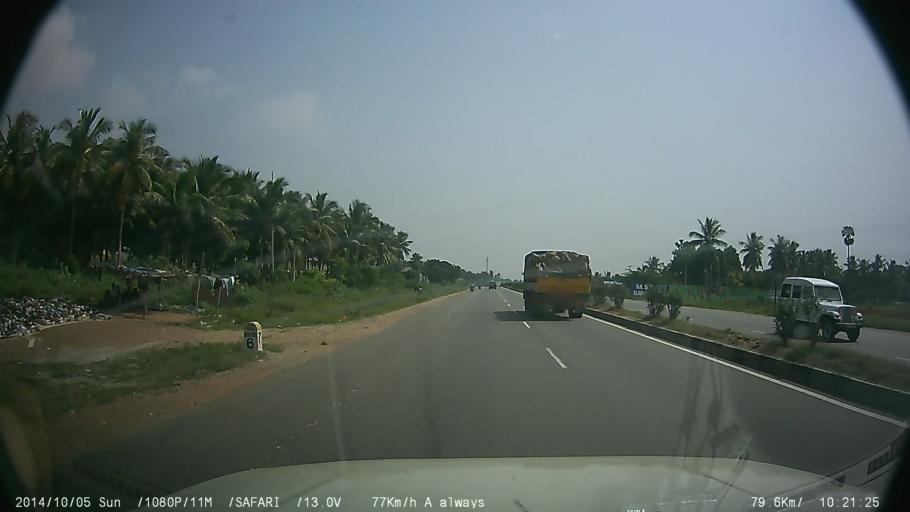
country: IN
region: Tamil Nadu
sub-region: Salem
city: Attayyampatti
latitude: 11.5996
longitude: 78.0891
